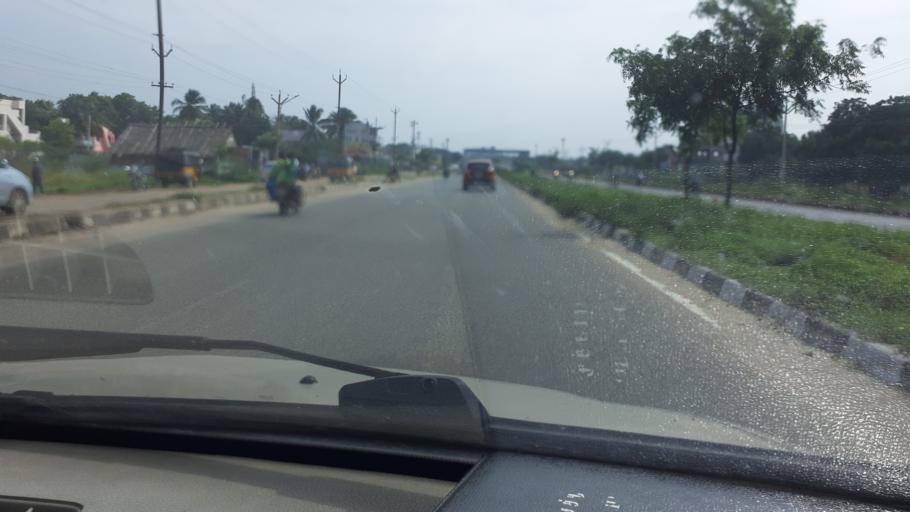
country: IN
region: Tamil Nadu
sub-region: Tirunelveli Kattabo
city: Tirunelveli
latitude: 8.7148
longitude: 77.7661
